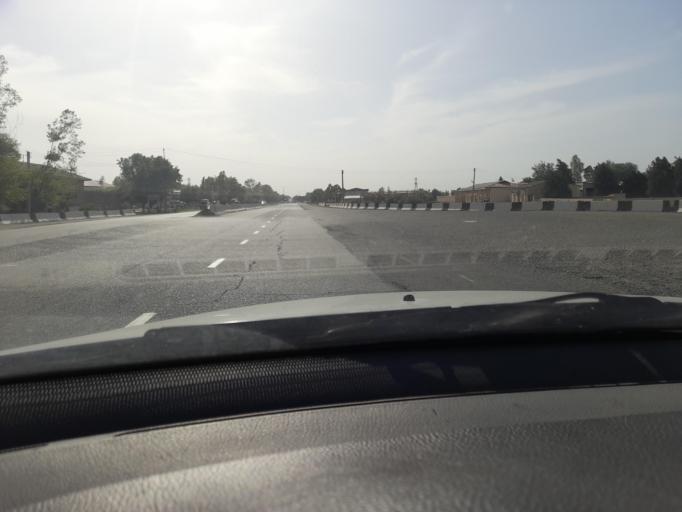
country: UZ
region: Samarqand
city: Kattaqo'rg'on
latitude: 39.9156
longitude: 66.3167
